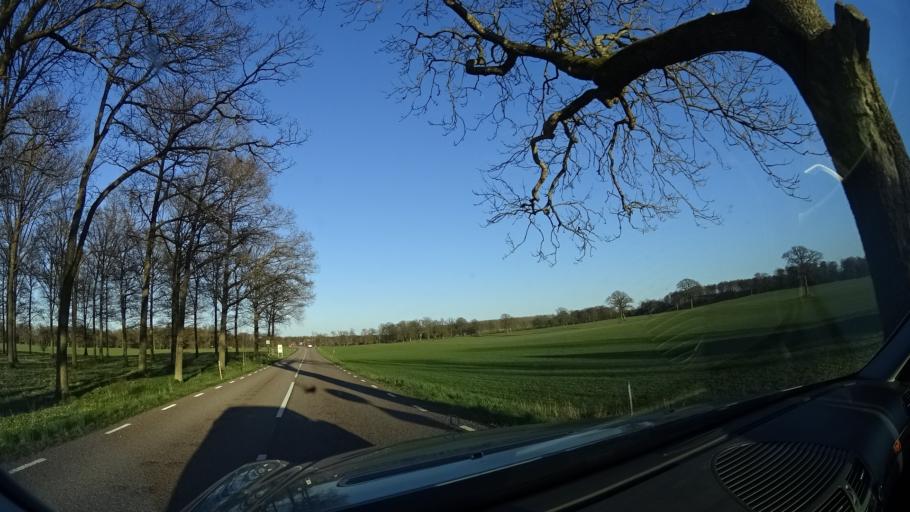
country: SE
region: Skane
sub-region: Svalovs Kommun
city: Kagerod
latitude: 55.9801
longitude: 13.1236
